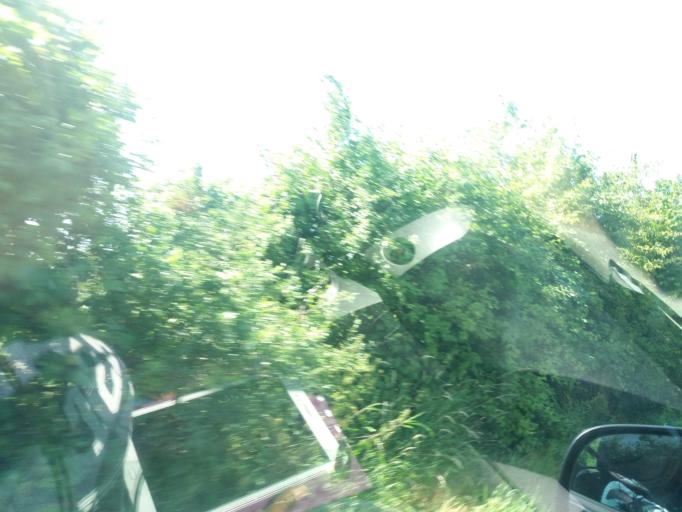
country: IE
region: Leinster
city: Balrothery
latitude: 53.5395
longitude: -6.2392
